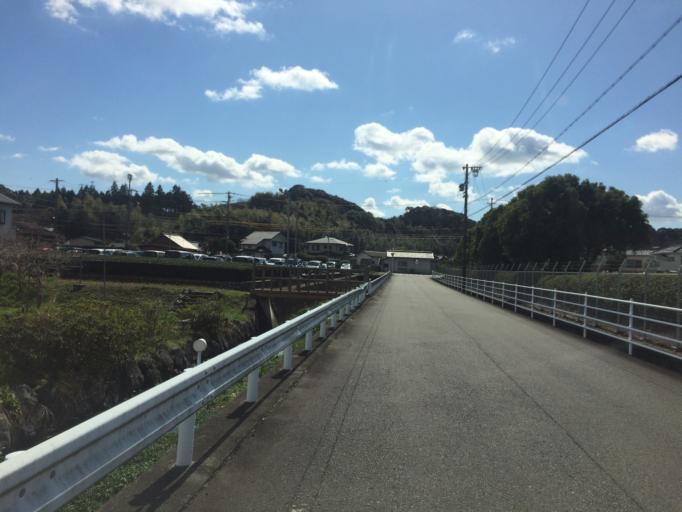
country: JP
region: Shizuoka
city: Shimada
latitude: 34.7600
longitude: 138.1949
